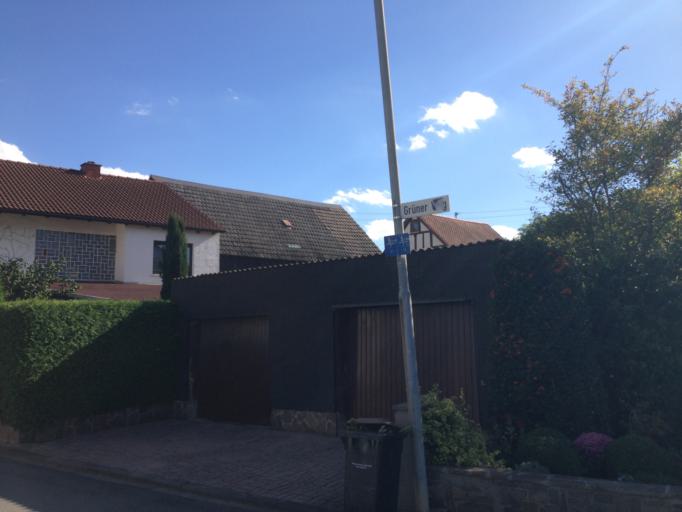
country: DE
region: Hesse
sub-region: Regierungsbezirk Giessen
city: Bischoffen
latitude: 50.6736
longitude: 8.5225
